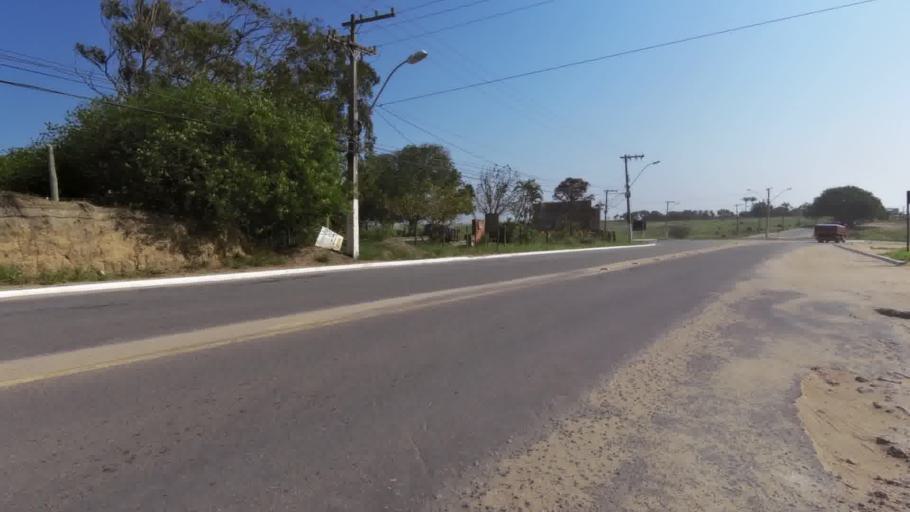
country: BR
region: Espirito Santo
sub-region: Marataizes
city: Marataizes
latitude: -21.0460
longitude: -40.8435
